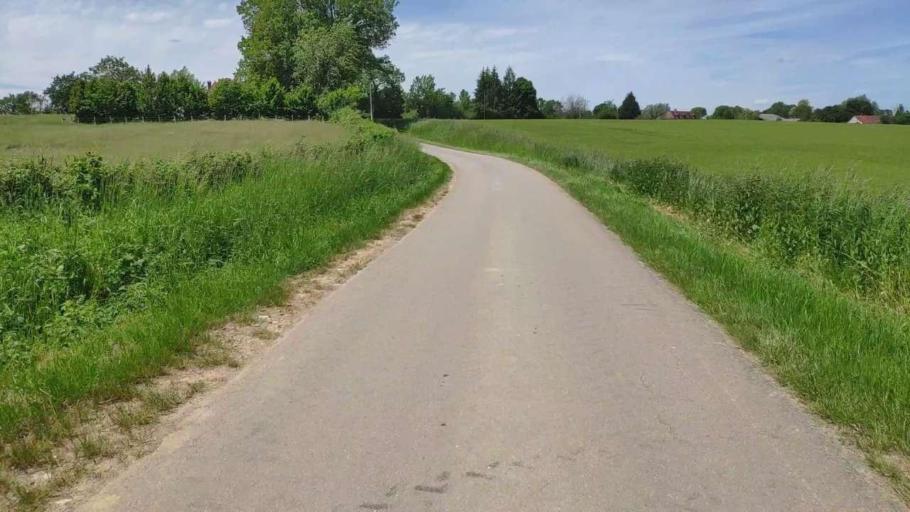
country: FR
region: Franche-Comte
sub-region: Departement du Jura
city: Bletterans
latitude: 46.7804
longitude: 5.3832
